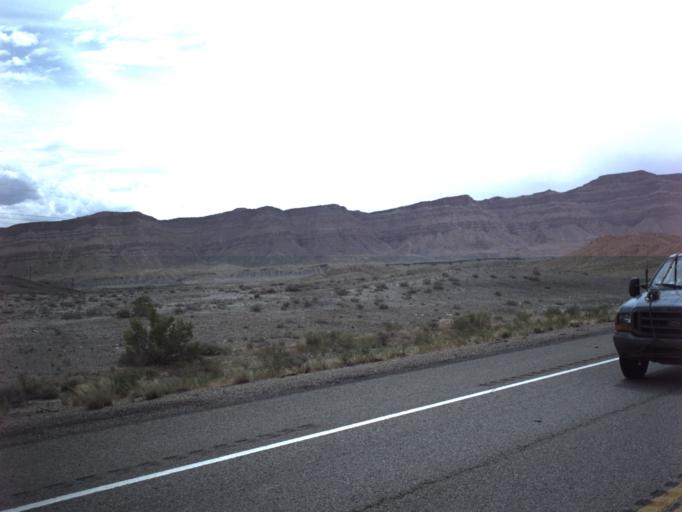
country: US
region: Utah
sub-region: Carbon County
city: East Carbon City
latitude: 39.2548
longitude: -110.3395
